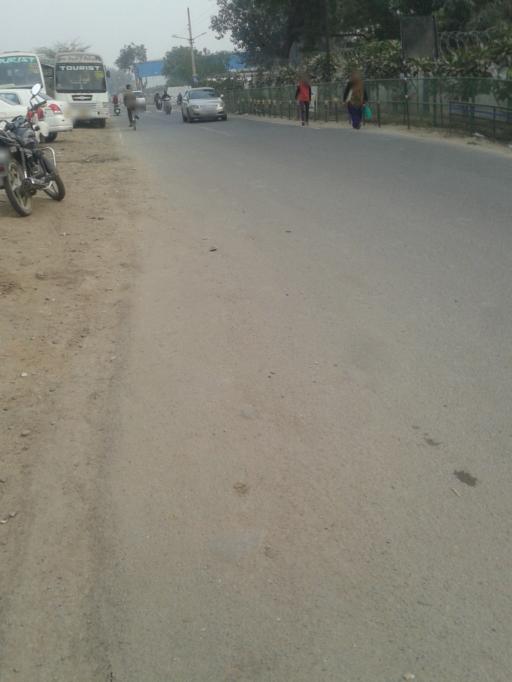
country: IN
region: NCT
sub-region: West Delhi
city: Nangloi Jat
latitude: 28.5789
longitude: 77.1005
